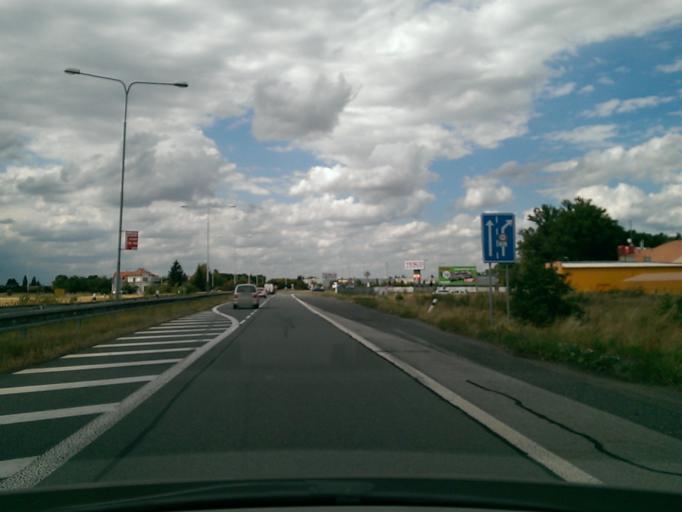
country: CZ
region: Central Bohemia
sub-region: Okres Nymburk
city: Podebrady
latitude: 50.1314
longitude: 15.0997
